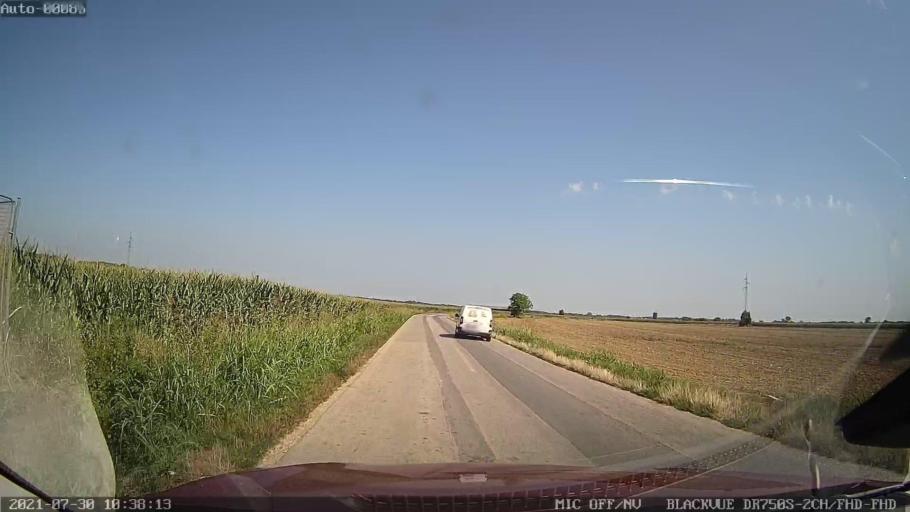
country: HR
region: Varazdinska
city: Jalzabet
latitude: 46.2592
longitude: 16.4339
